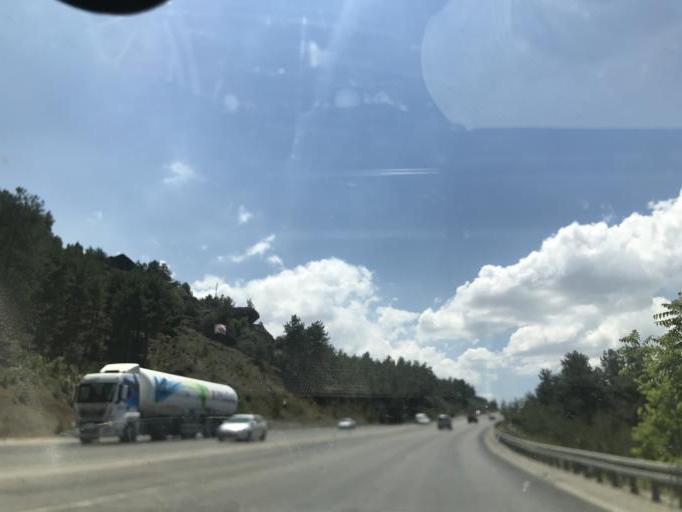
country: TR
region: Denizli
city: Serinhisar
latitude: 37.6500
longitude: 29.2259
